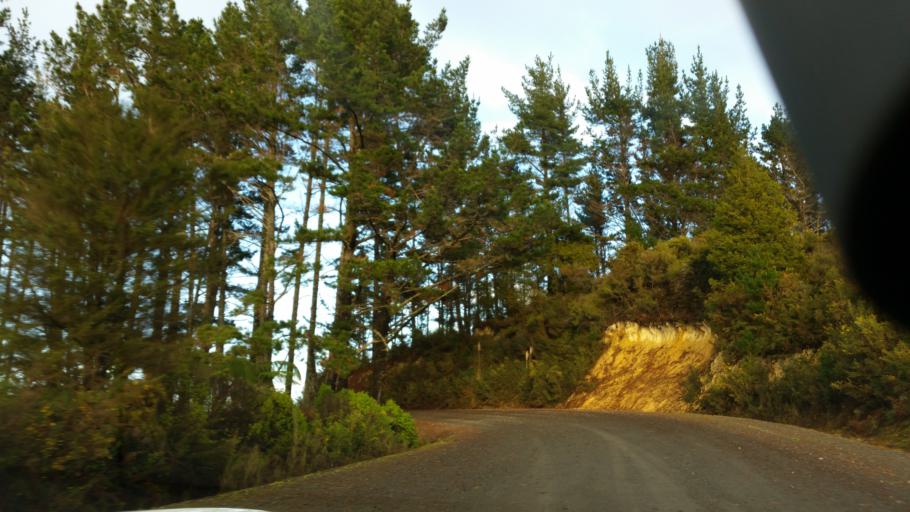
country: NZ
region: Northland
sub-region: Whangarei
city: Maungatapere
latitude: -35.7602
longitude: 174.0818
